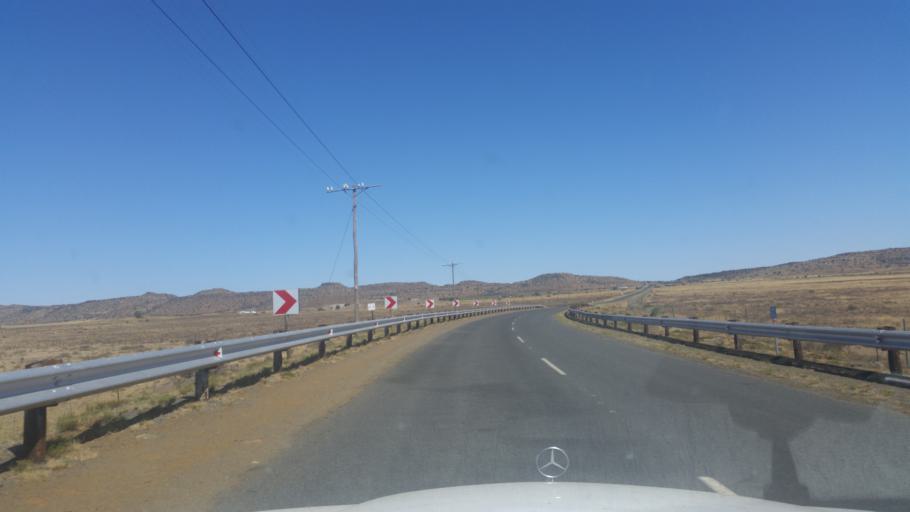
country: ZA
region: Eastern Cape
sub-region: Joe Gqabi District Municipality
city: Burgersdorp
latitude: -30.7839
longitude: 25.7780
